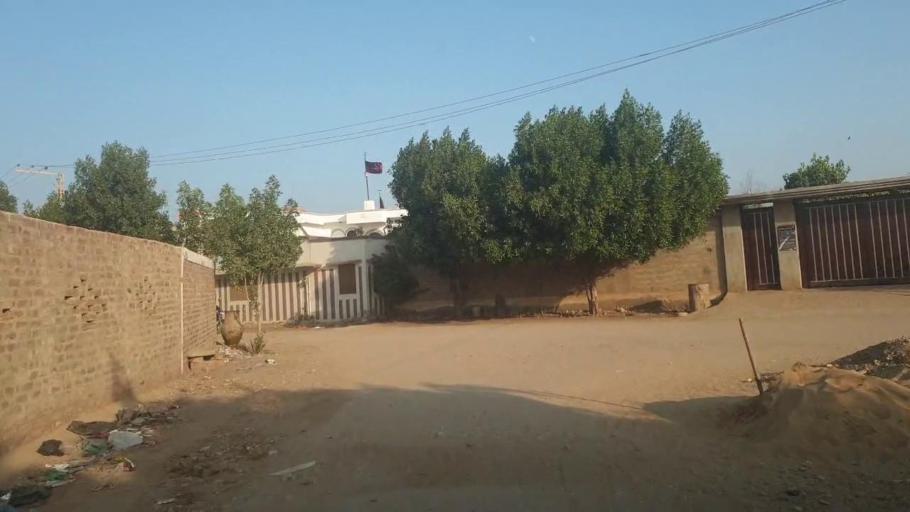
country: PK
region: Sindh
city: Jamshoro
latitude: 25.4422
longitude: 68.2924
